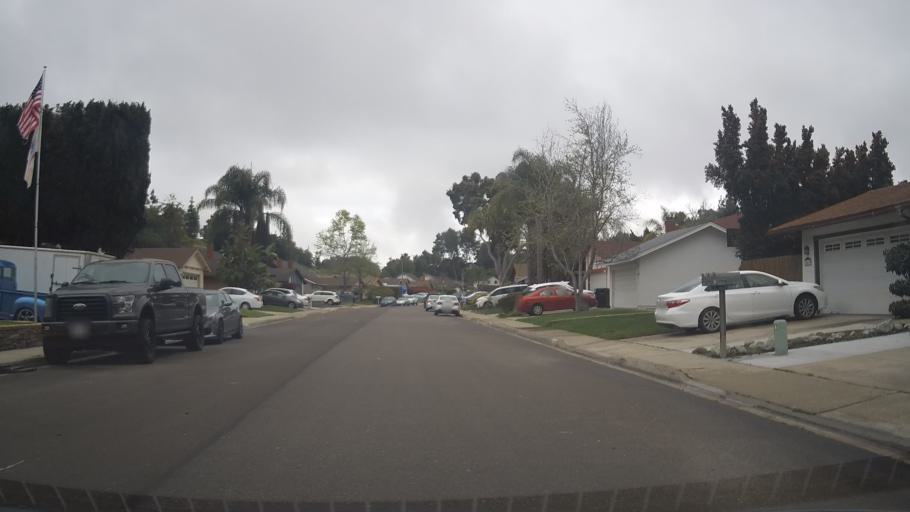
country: US
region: California
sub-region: San Diego County
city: Poway
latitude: 32.9960
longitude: -117.0855
